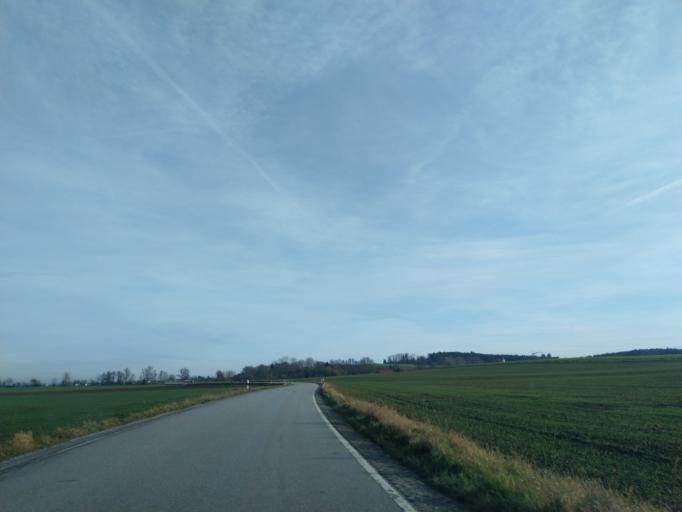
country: DE
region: Bavaria
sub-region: Lower Bavaria
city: Wallerfing
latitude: 48.6907
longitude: 12.8563
